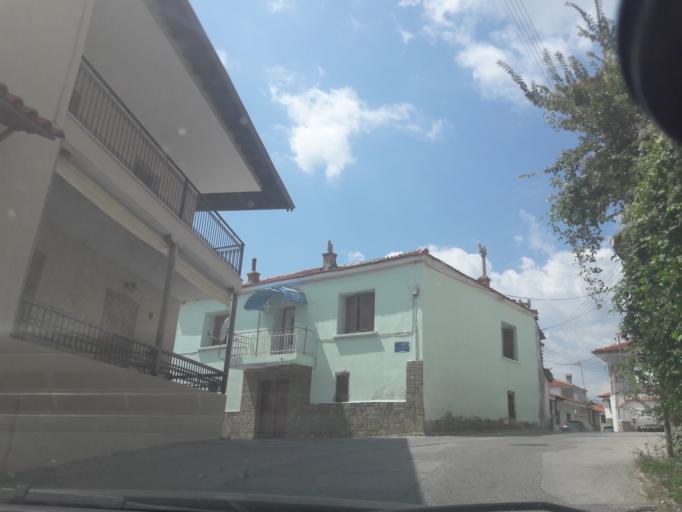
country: GR
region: Central Macedonia
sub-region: Nomos Chalkidikis
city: Polygyros
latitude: 40.3761
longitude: 23.4398
